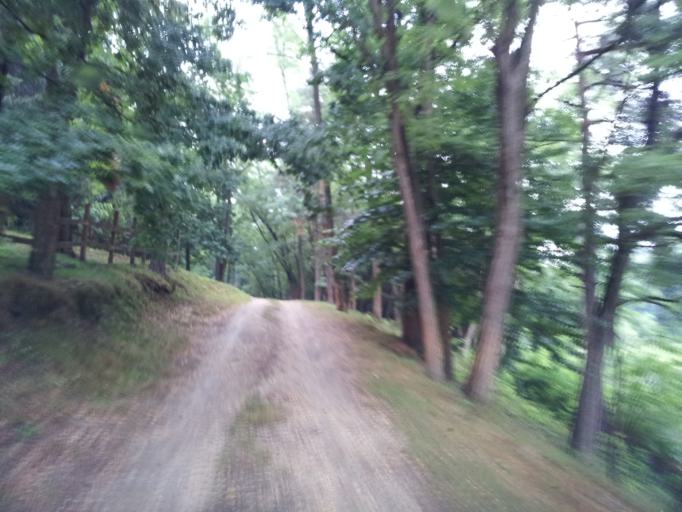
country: HU
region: Zala
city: Zalalovo
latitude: 46.8787
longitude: 16.5511
